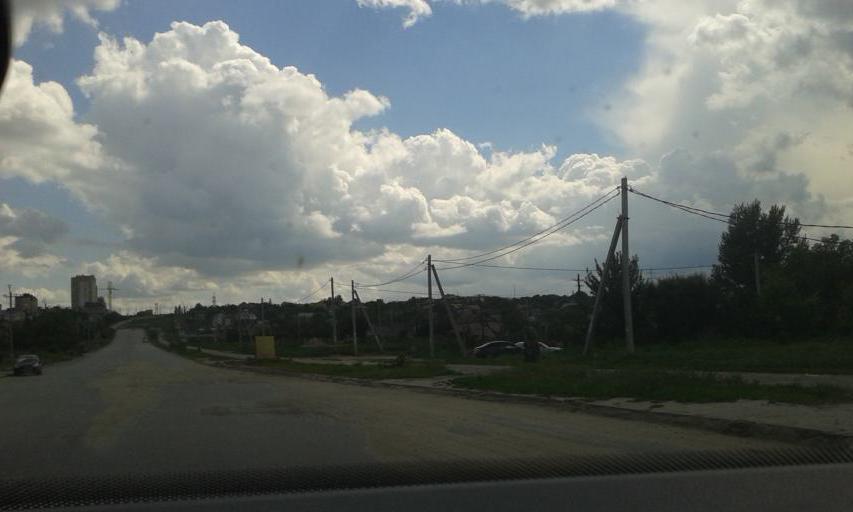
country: RU
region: Volgograd
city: Volgograd
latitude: 48.6553
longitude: 44.4134
